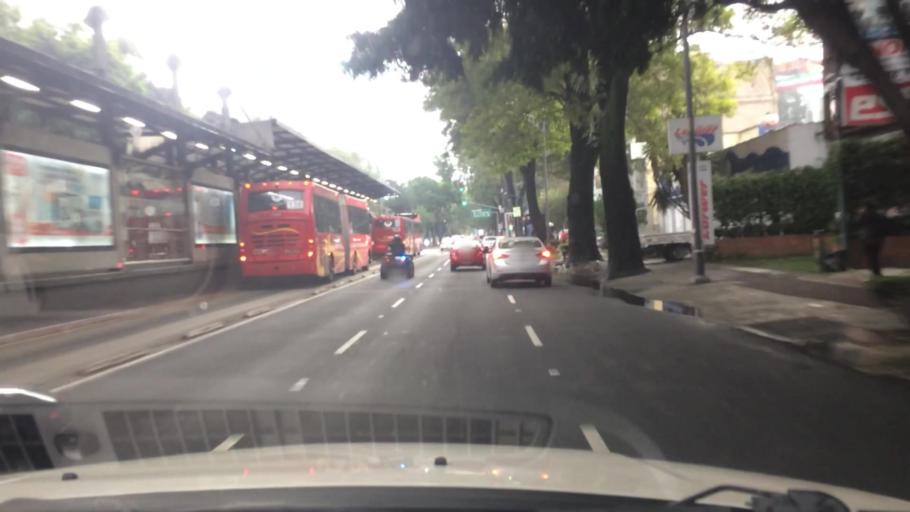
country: MX
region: Mexico City
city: Alvaro Obregon
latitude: 19.3582
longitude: -99.1840
